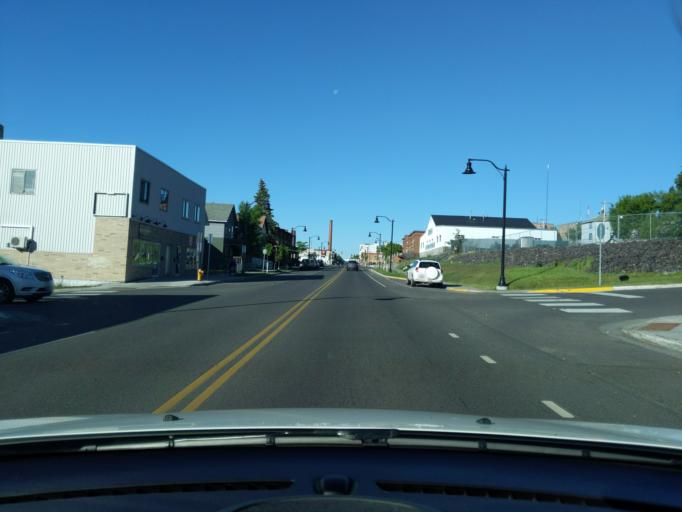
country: US
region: Minnesota
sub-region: Saint Louis County
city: Duluth
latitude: 46.7975
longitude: -92.0924
